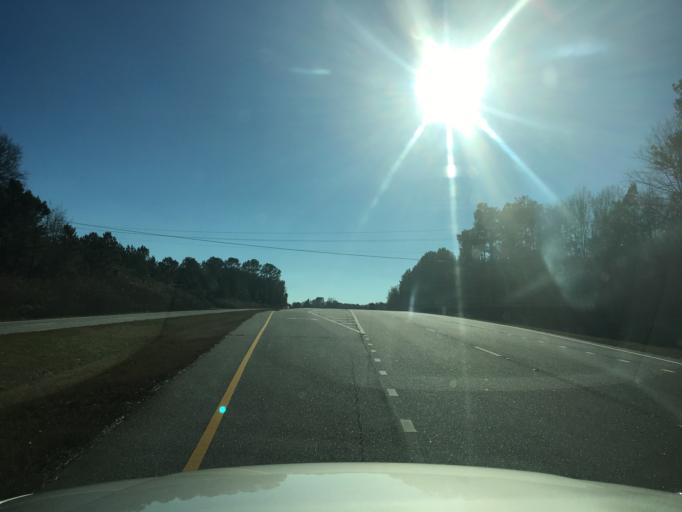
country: US
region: Georgia
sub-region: Carroll County
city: Carrollton
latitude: 33.4423
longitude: -85.1298
